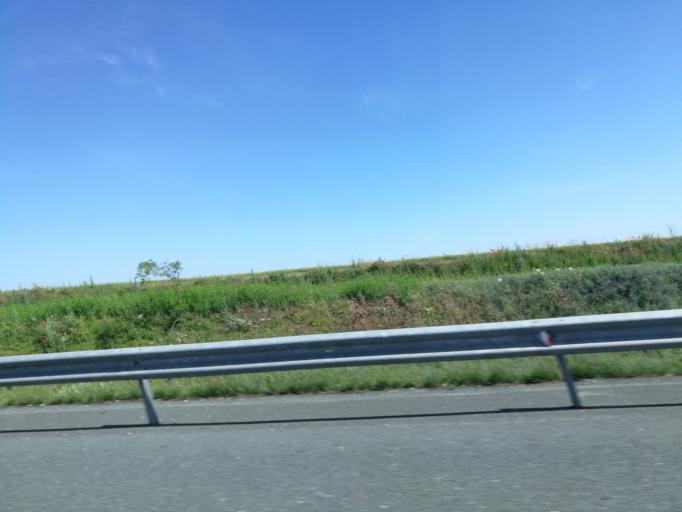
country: RO
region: Constanta
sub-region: Comuna Baraganu
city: Baraganu
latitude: 44.1333
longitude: 28.3944
